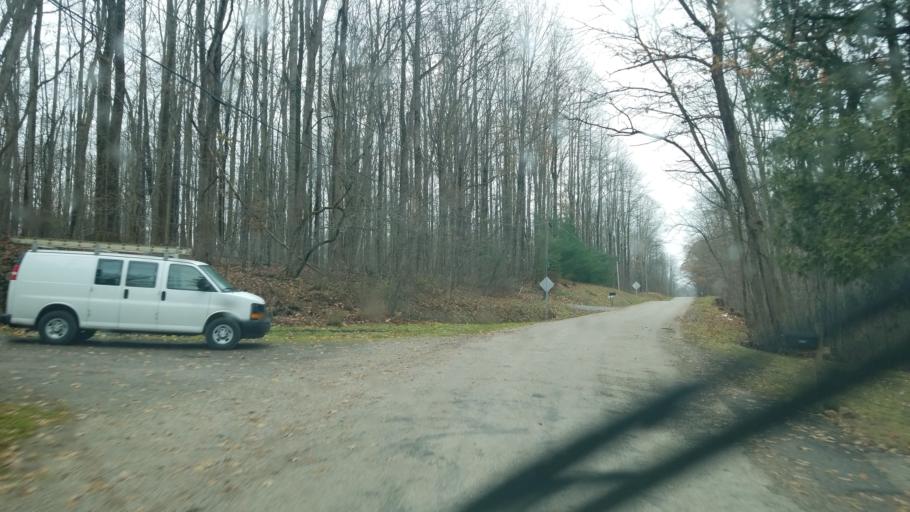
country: US
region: Ohio
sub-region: Ashtabula County
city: Geneva
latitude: 41.7563
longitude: -80.8742
